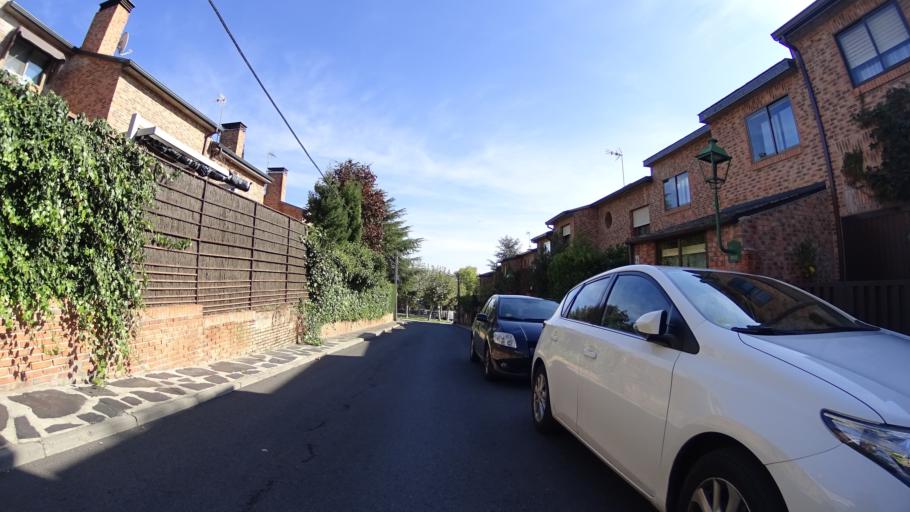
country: ES
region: Madrid
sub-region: Provincia de Madrid
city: Navalquejigo
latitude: 40.6073
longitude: -4.0294
